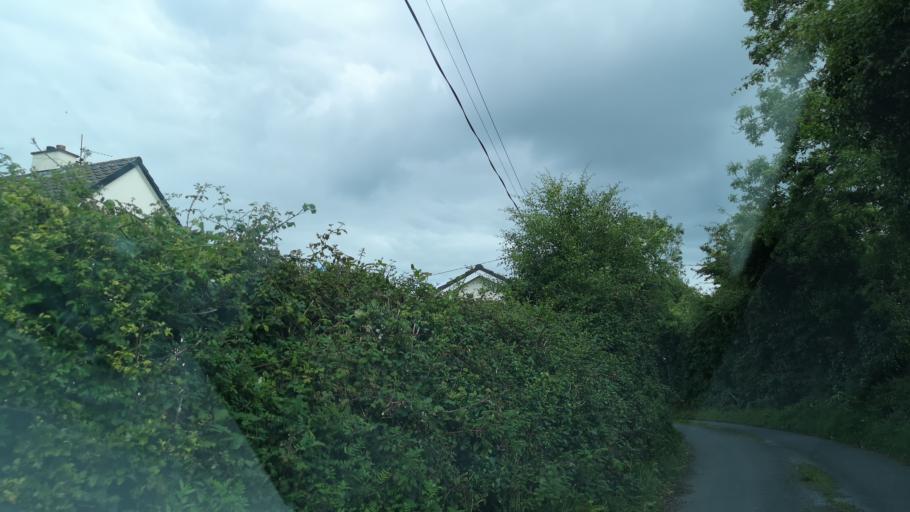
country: IE
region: Connaught
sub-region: County Galway
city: Moycullen
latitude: 53.3207
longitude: -9.1458
